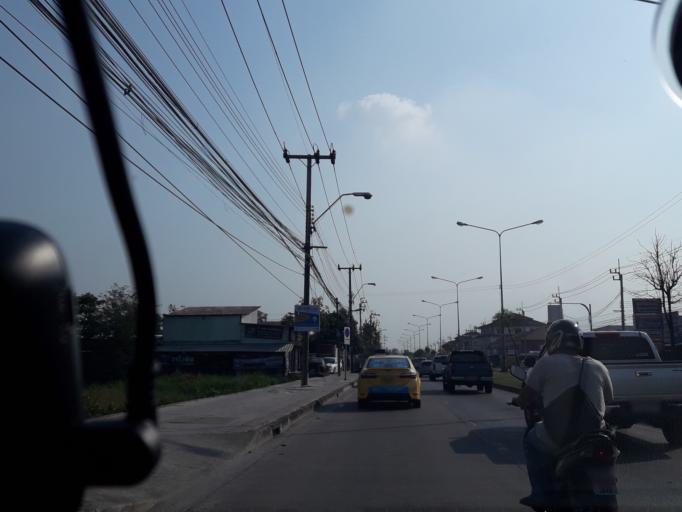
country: TH
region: Bangkok
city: Khlong Sam Wa
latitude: 13.8679
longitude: 100.7226
